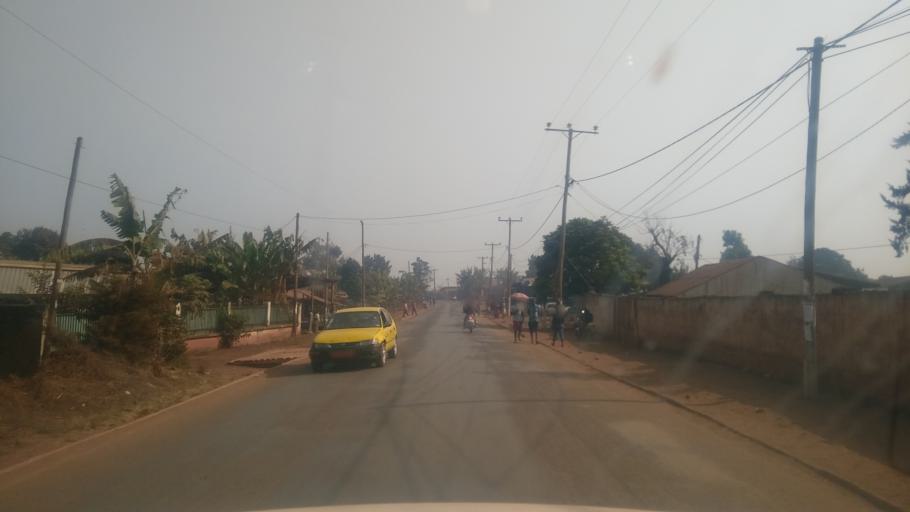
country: CM
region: West
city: Bafoussam
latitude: 5.5003
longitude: 10.3971
